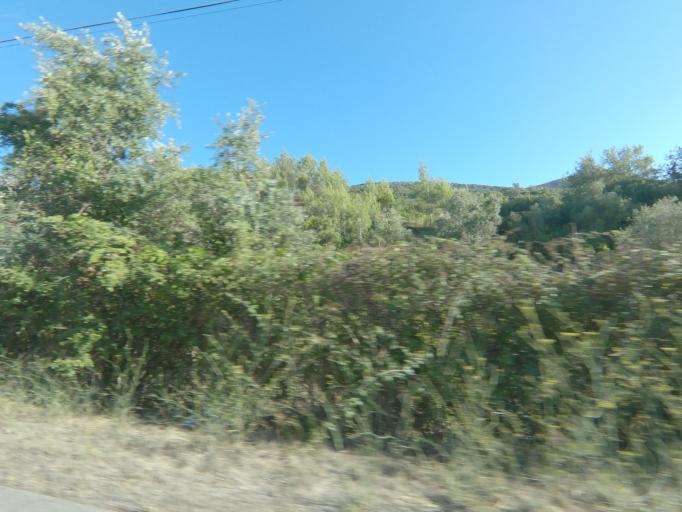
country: PT
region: Setubal
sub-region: Palmela
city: Quinta do Anjo
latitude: 38.5035
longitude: -8.9648
